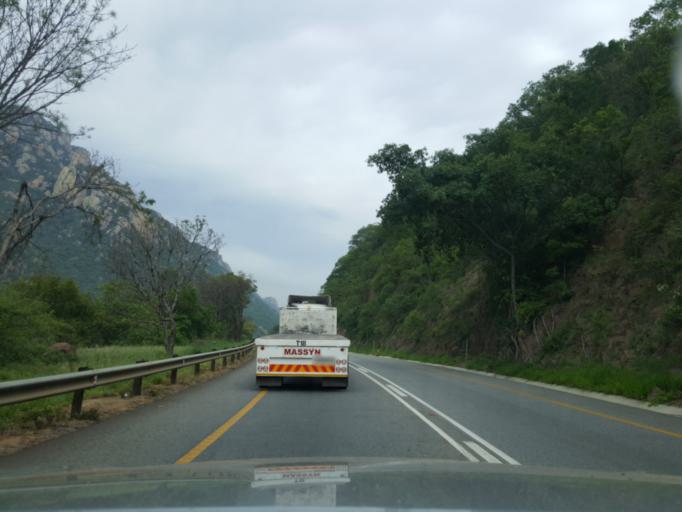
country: ZA
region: Mpumalanga
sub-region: Ehlanzeni District
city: Nelspruit
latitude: -25.5189
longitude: 31.2421
